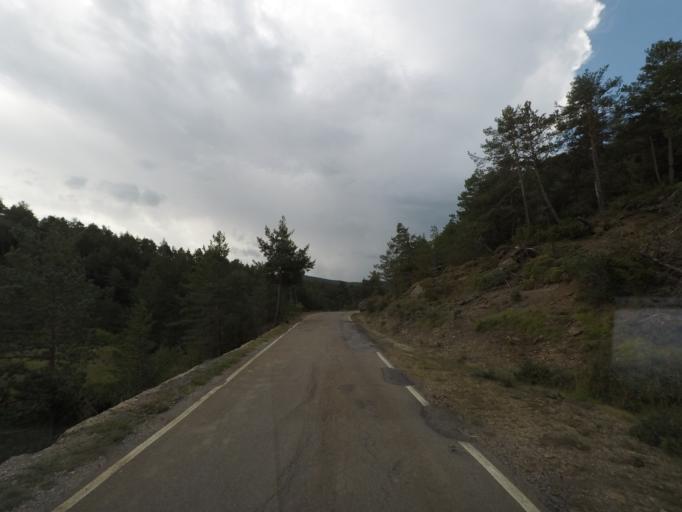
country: ES
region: Aragon
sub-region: Provincia de Huesca
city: Fiscal
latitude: 42.4048
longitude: -0.0707
